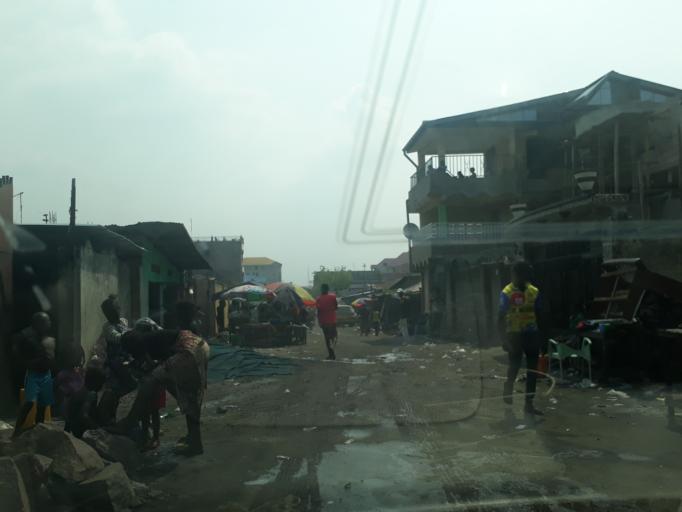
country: CD
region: Kinshasa
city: Kinshasa
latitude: -4.3248
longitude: 15.3159
